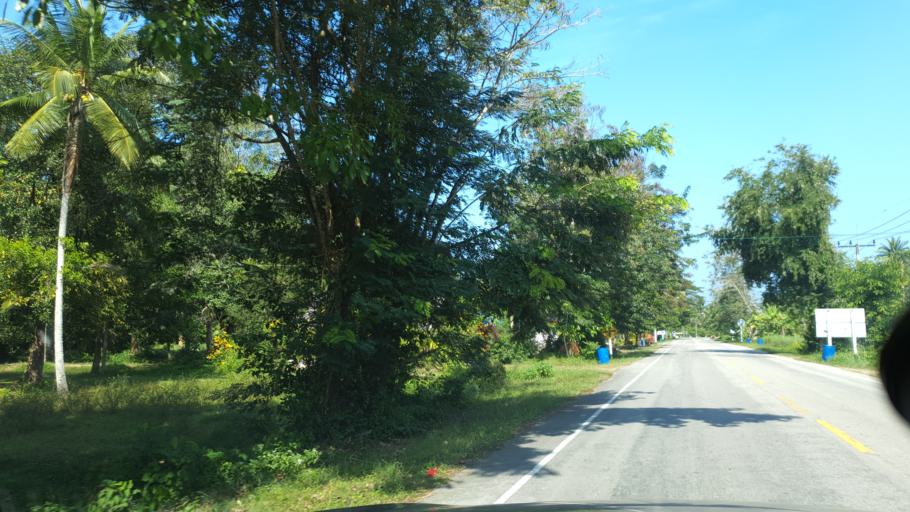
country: TH
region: Surat Thani
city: Tha Chana
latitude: 9.5855
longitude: 99.2000
